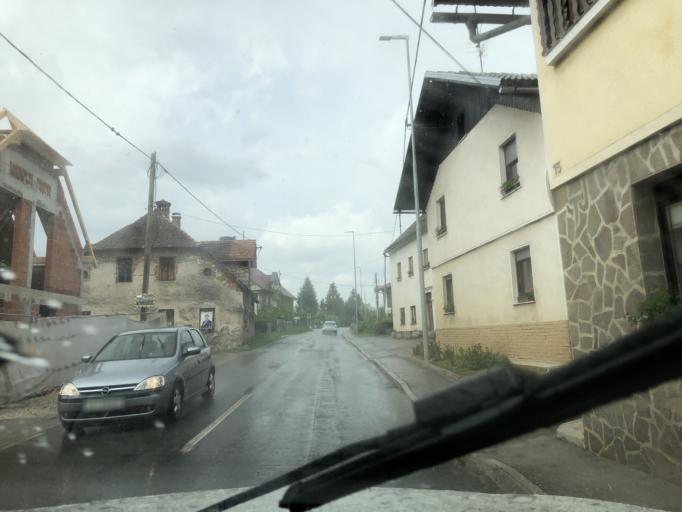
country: SI
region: Cerknica
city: Cerknica
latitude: 45.7757
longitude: 14.4032
